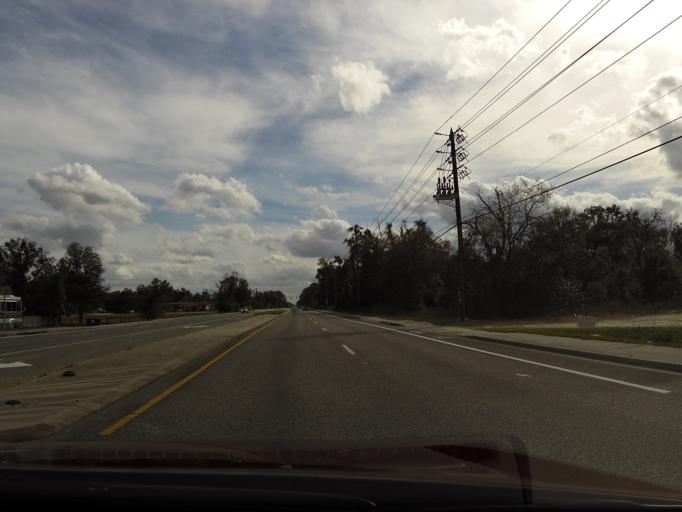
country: US
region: Florida
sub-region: Volusia County
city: North DeLand
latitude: 29.0571
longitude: -81.3252
